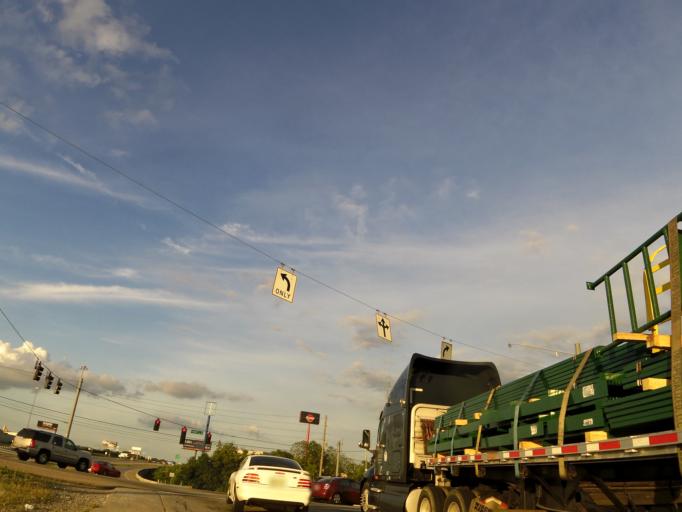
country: US
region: Tennessee
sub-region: Knox County
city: Farragut
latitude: 35.9055
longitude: -84.1449
